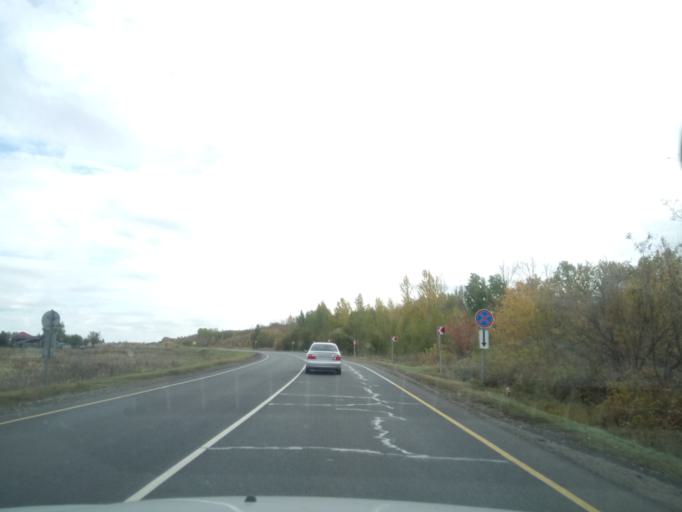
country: RU
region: Nizjnij Novgorod
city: Lukoyanov
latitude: 55.0506
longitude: 44.3765
